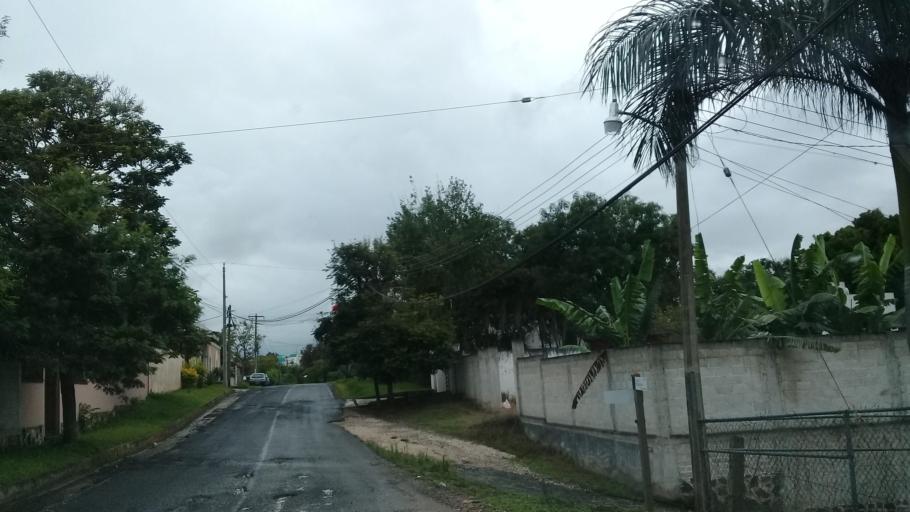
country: MX
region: Veracruz
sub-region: Emiliano Zapata
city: Jacarandas
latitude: 19.5047
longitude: -96.8433
